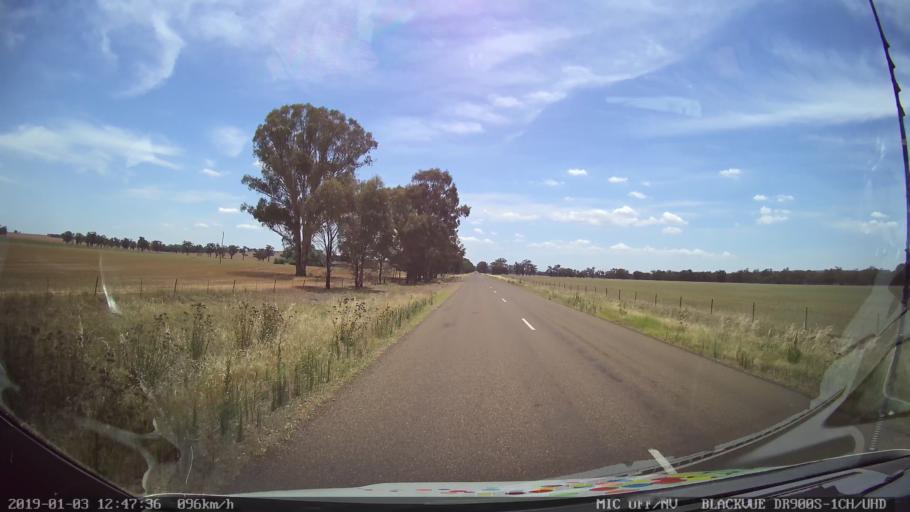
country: AU
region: New South Wales
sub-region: Weddin
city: Grenfell
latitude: -33.7248
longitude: 148.2433
